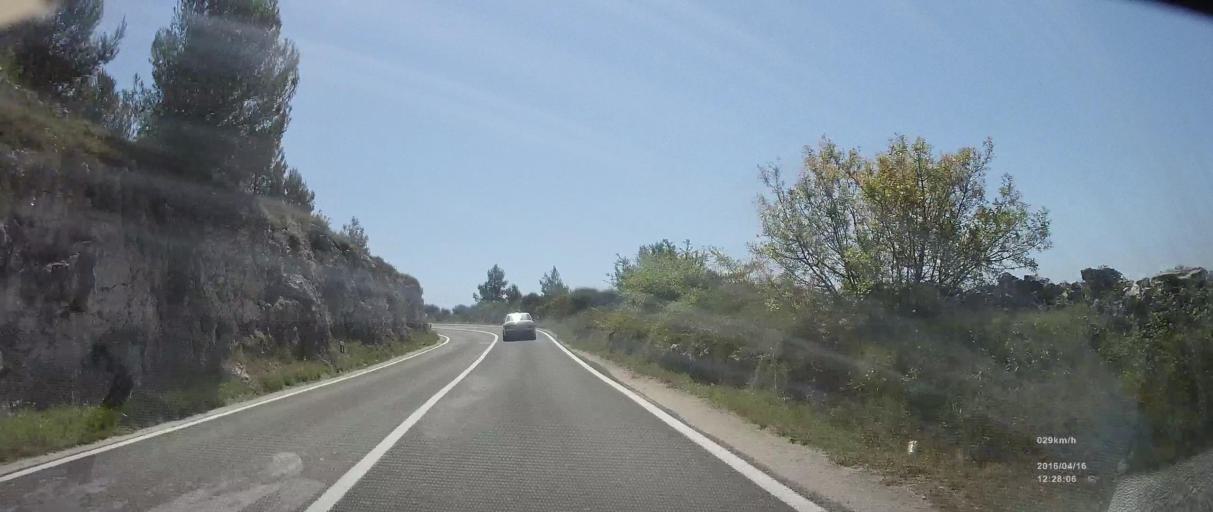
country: HR
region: Splitsko-Dalmatinska
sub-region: Grad Trogir
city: Trogir
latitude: 43.5205
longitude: 16.2080
